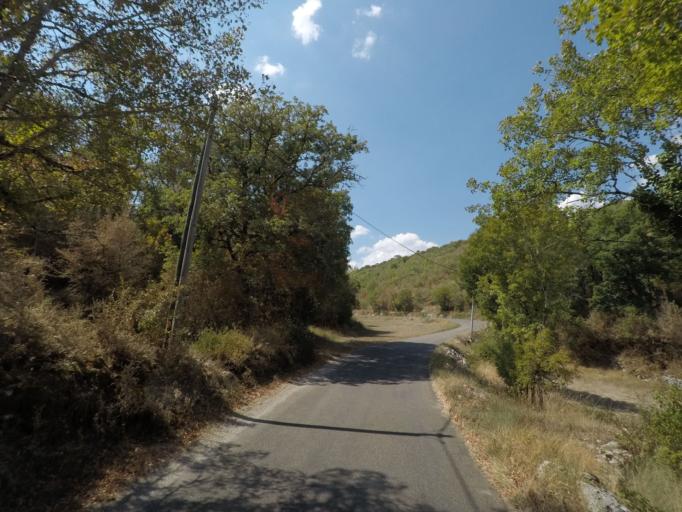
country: FR
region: Midi-Pyrenees
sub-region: Departement du Lot
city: Lalbenque
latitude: 44.5165
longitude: 1.6420
